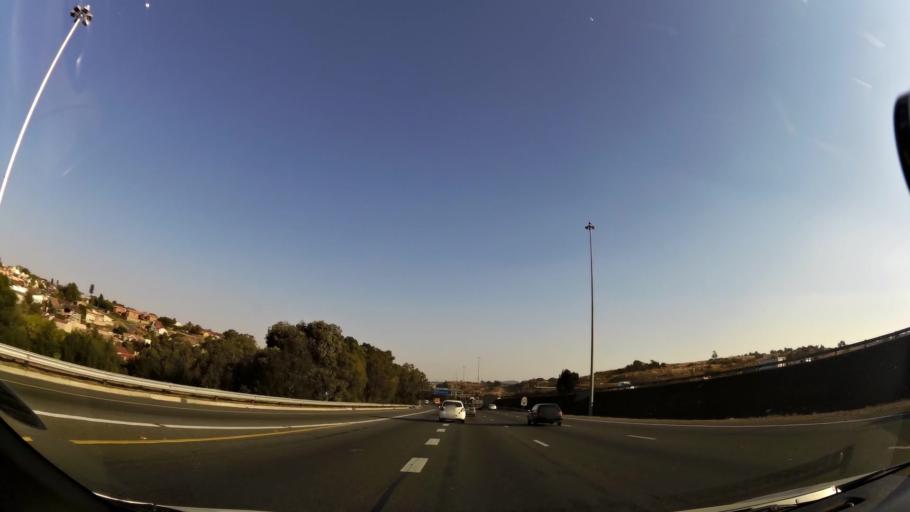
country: ZA
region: Gauteng
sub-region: Ekurhuleni Metropolitan Municipality
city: Germiston
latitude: -26.2460
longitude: 28.1241
